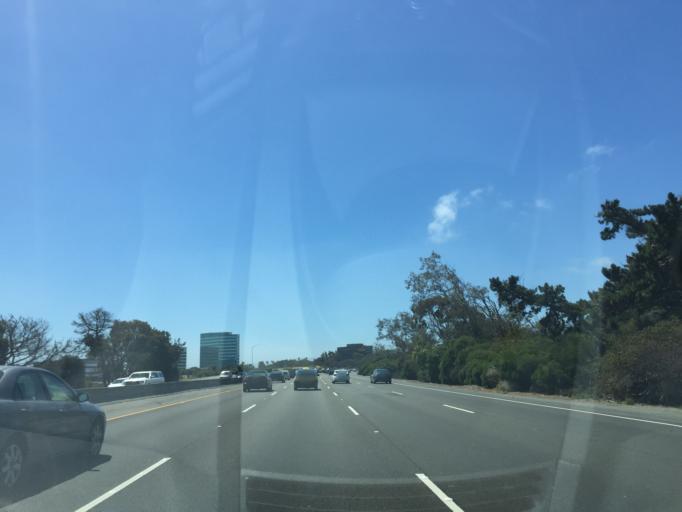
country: US
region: California
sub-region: San Mateo County
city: Brisbane
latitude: 37.6811
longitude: -122.3890
